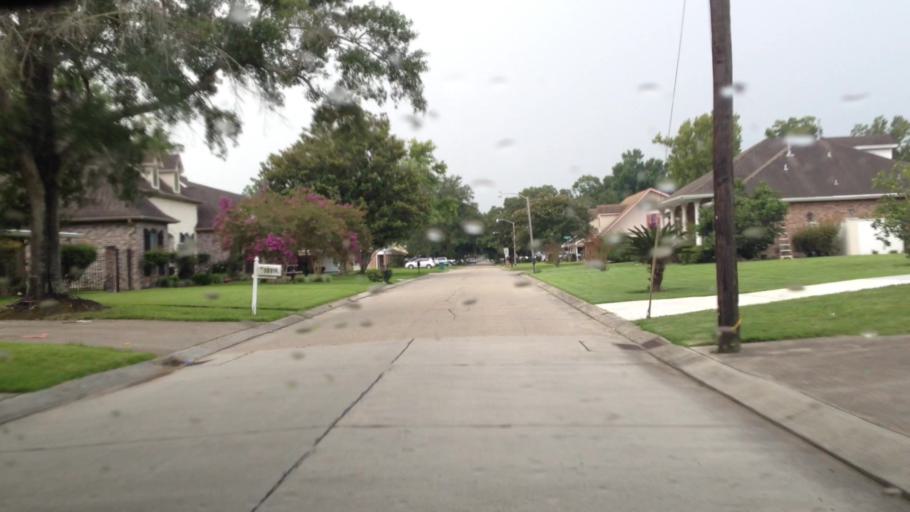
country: US
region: Louisiana
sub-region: Jefferson Parish
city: Jefferson
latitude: 29.9480
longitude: -90.1550
